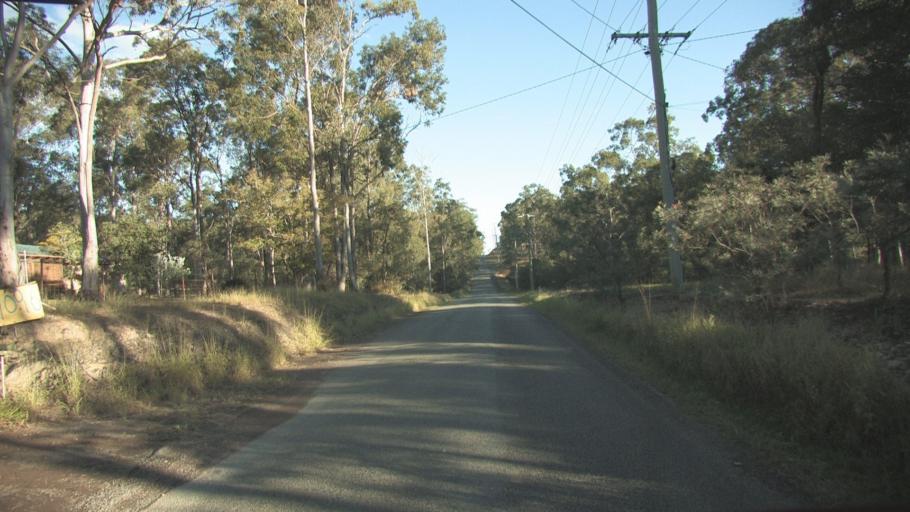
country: AU
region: Queensland
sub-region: Logan
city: Waterford West
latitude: -27.7271
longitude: 153.1528
